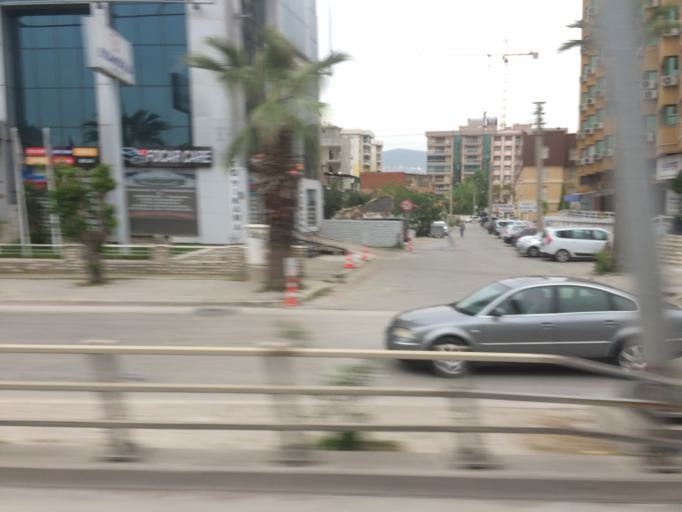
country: TR
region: Izmir
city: Buca
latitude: 38.4495
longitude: 27.1838
